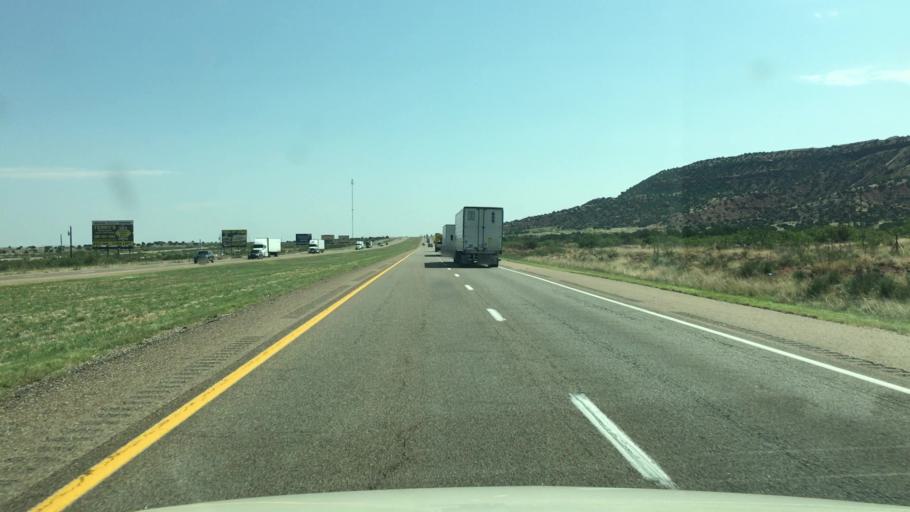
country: US
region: New Mexico
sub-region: Guadalupe County
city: Santa Rosa
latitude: 35.0380
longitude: -104.3943
